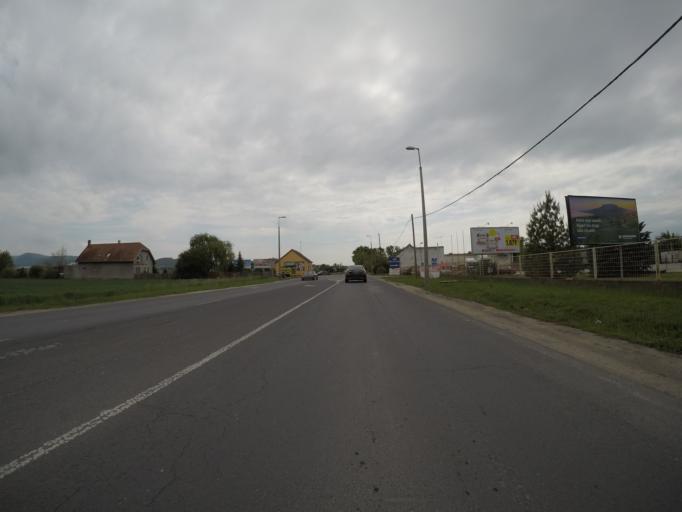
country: HU
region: Komarom-Esztergom
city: Esztergom
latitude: 47.7720
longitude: 18.7379
